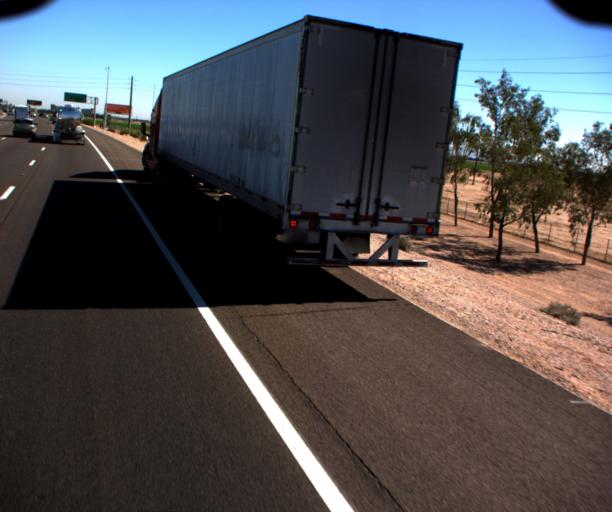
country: US
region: Arizona
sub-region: Maricopa County
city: Avondale
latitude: 33.4575
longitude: -112.3186
